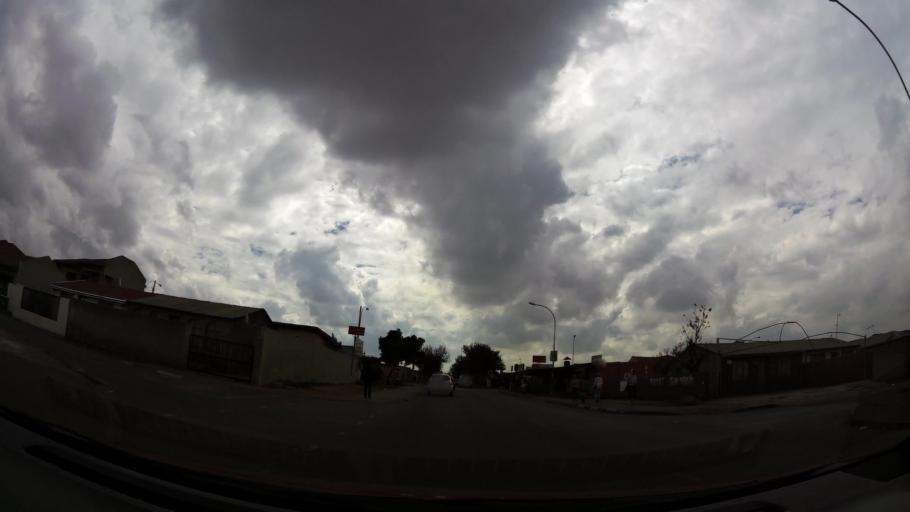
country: ZA
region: Gauteng
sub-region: City of Johannesburg Metropolitan Municipality
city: Soweto
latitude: -26.2493
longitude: 27.8316
